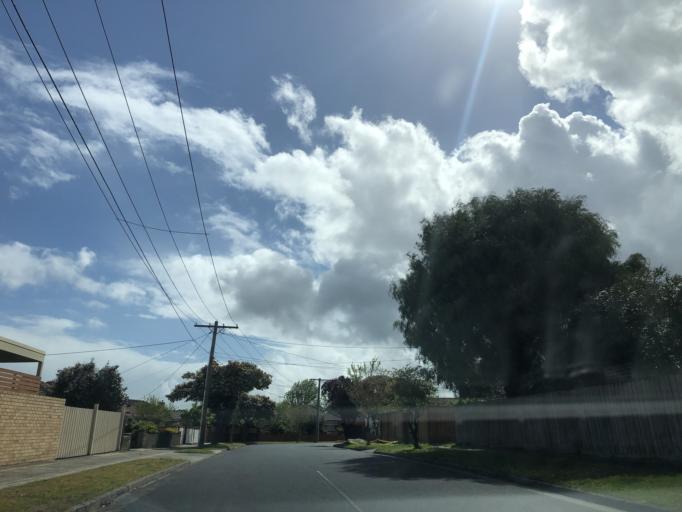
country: AU
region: Victoria
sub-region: Kingston
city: Clayton South
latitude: -37.9289
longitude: 145.1094
